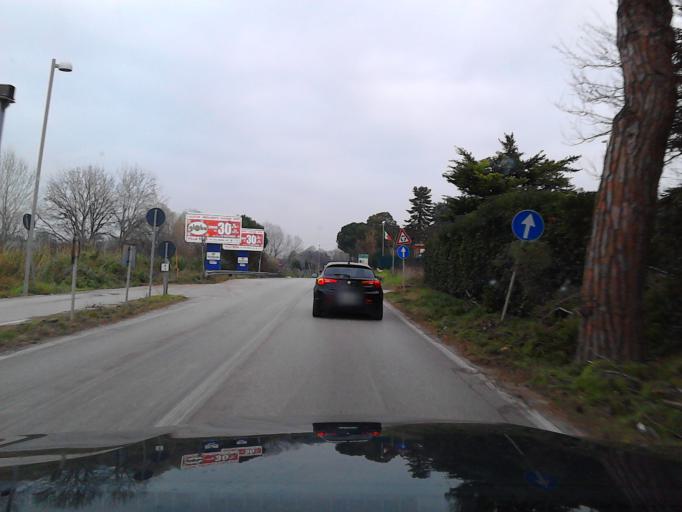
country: IT
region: Abruzzo
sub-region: Provincia di Teramo
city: Alba Adriatica
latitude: 42.8334
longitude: 13.9008
